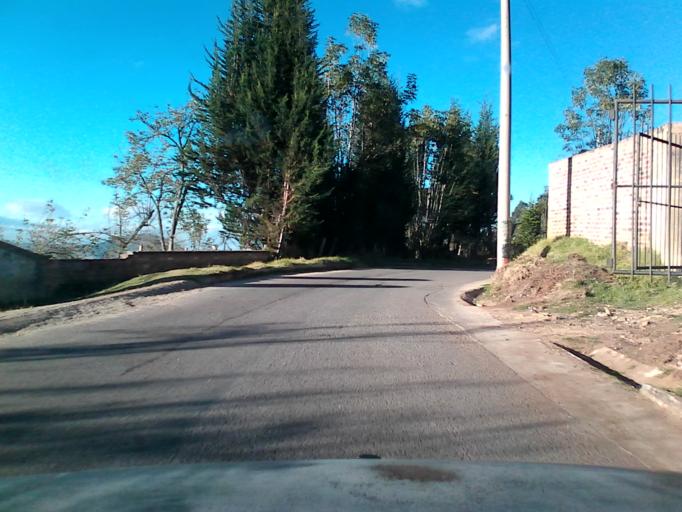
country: CO
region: Boyaca
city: Duitama
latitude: 5.8610
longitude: -73.0336
